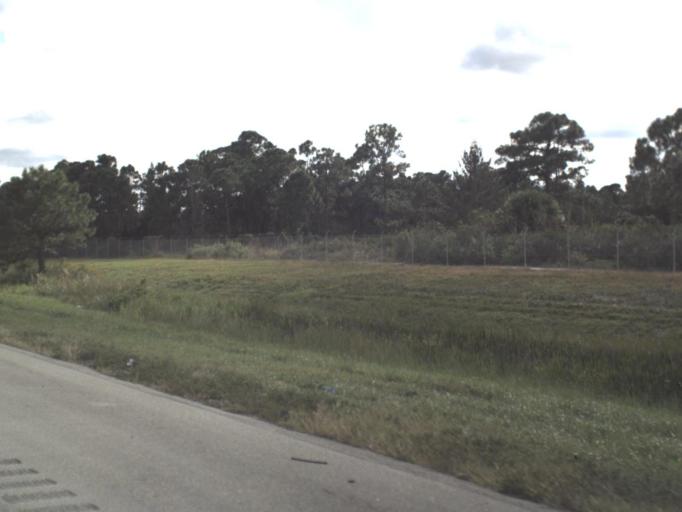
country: US
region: Florida
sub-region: Saint Lucie County
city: Port Saint Lucie
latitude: 27.2563
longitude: -80.3495
